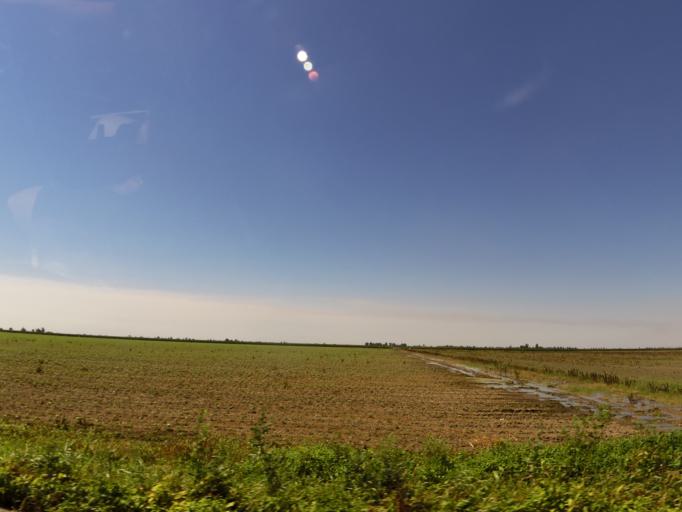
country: US
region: Missouri
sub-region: Dunklin County
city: Malden
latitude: 36.5531
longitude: -89.8617
